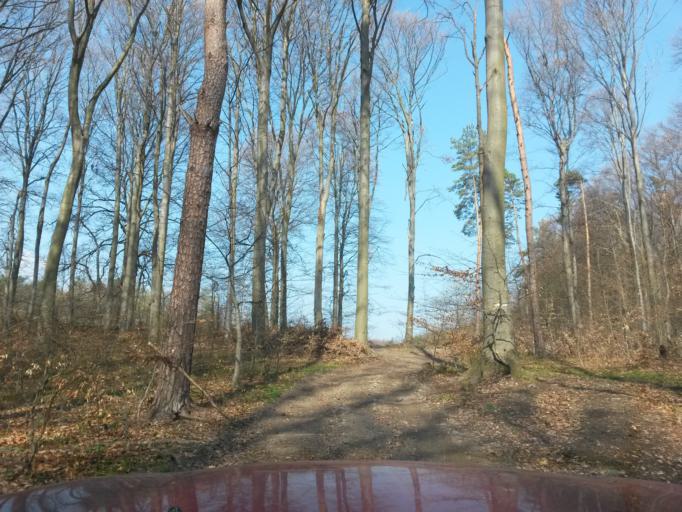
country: SK
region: Presovsky
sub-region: Okres Presov
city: Presov
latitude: 48.9290
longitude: 21.1538
